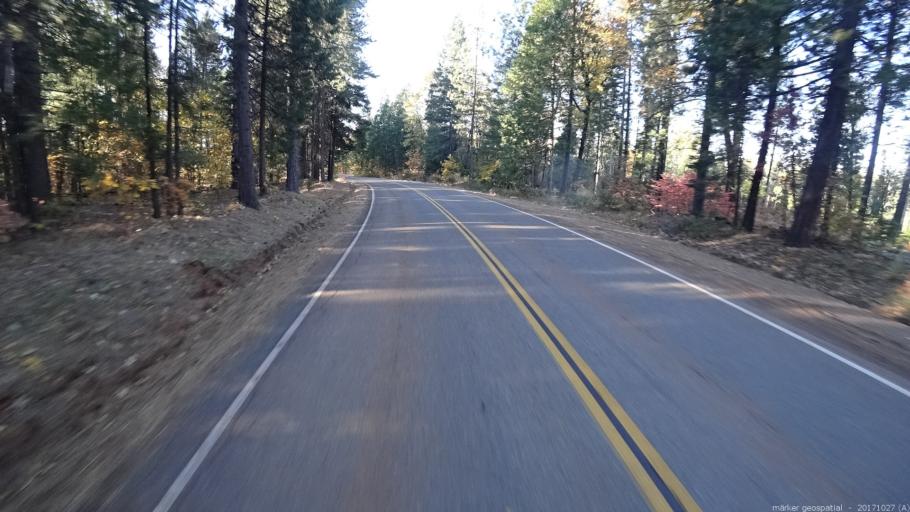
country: US
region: California
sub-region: Shasta County
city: Burney
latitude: 40.9615
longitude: -121.9408
